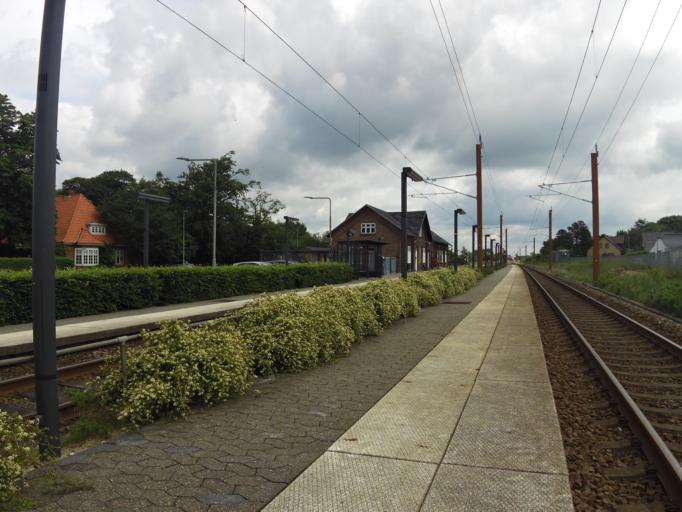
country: DK
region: South Denmark
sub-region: Vejen Kommune
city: Holsted
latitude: 55.4848
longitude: 8.9133
